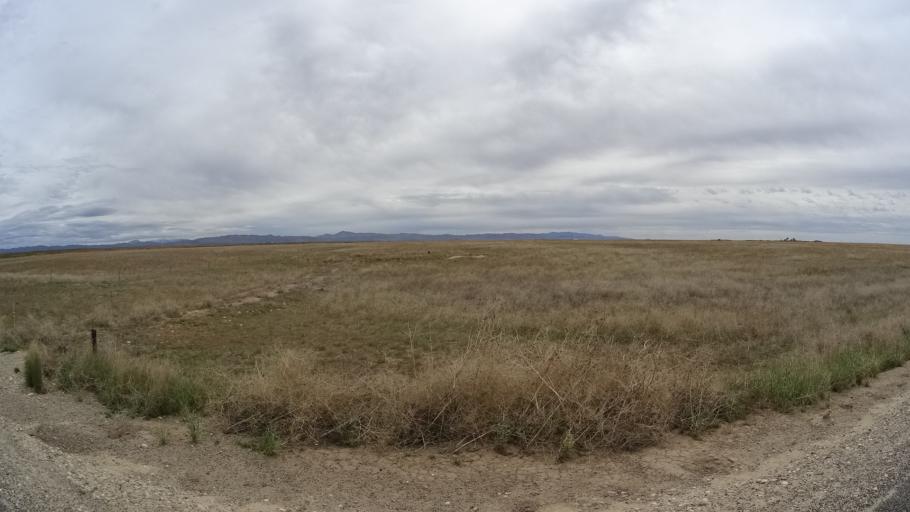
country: US
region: Idaho
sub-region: Ada County
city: Boise
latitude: 43.3538
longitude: -116.0049
